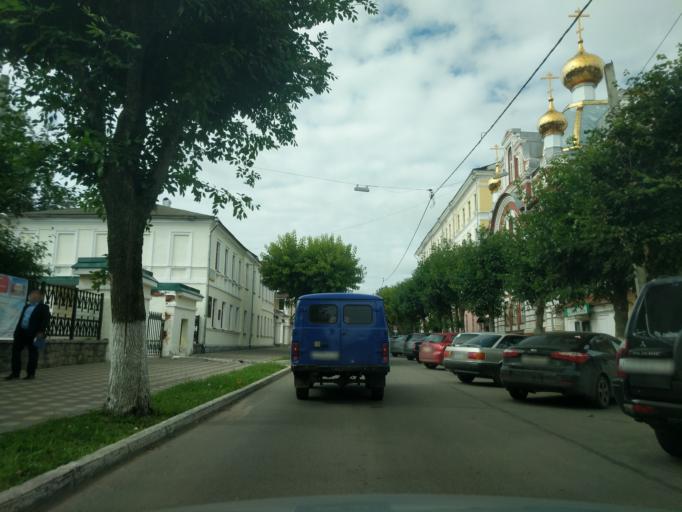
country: RU
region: Kirov
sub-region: Kirovo-Chepetskiy Rayon
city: Kirov
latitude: 58.6035
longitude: 49.6713
